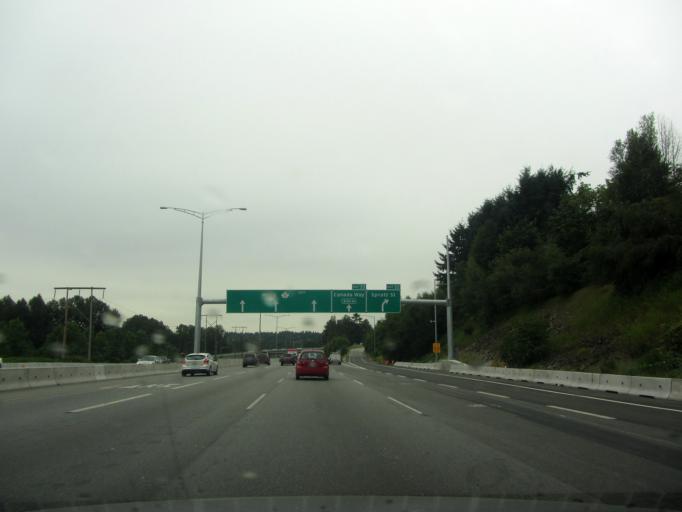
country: CA
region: British Columbia
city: Burnaby
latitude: 49.2576
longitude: -123.0115
